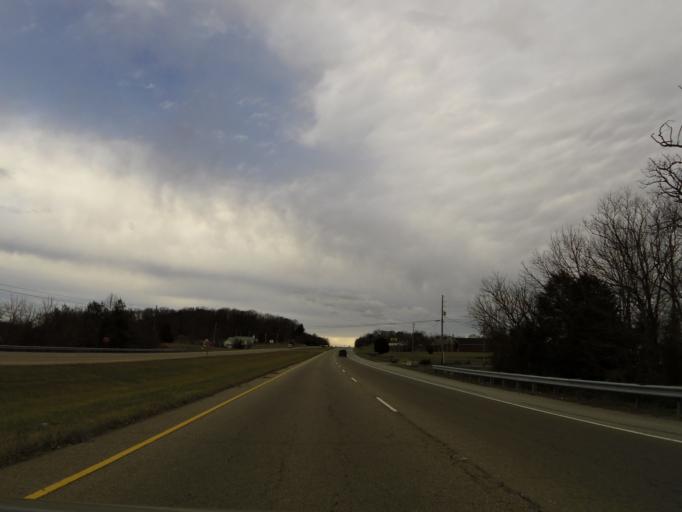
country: US
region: Tennessee
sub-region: Greene County
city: Tusculum
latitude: 36.2186
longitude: -82.7052
